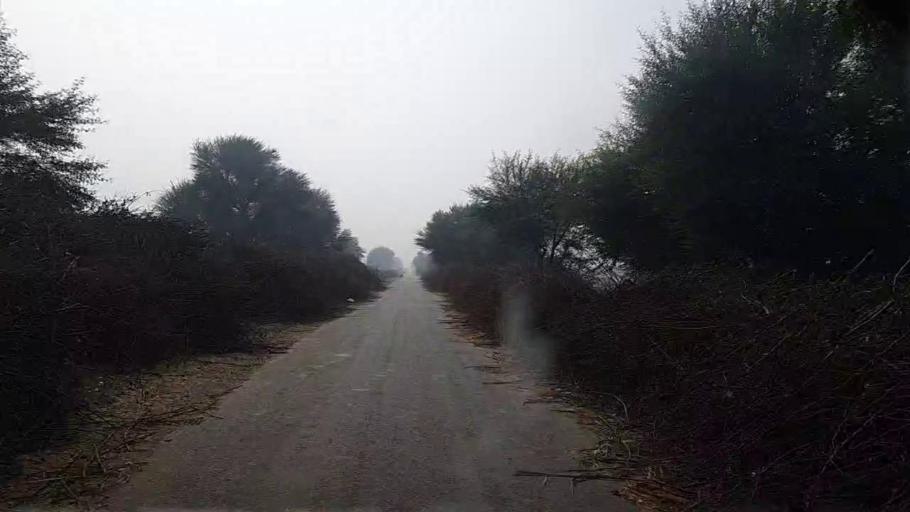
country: PK
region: Sindh
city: Kandiari
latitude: 26.9892
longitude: 68.6042
